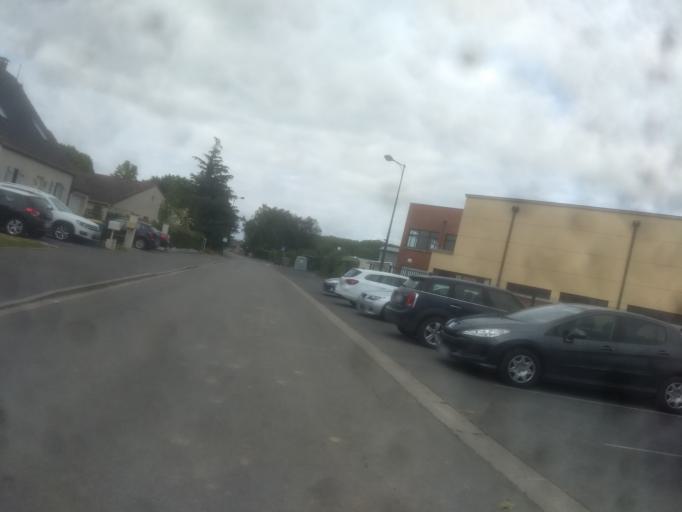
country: FR
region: Nord-Pas-de-Calais
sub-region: Departement du Pas-de-Calais
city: Tilloy-les-Mofflaines
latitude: 50.2704
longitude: 2.8169
